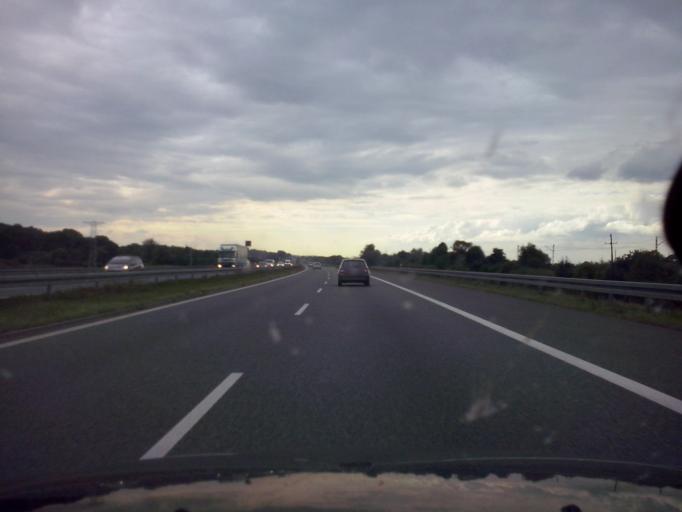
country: PL
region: Lesser Poland Voivodeship
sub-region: Powiat wielicki
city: Wegrzce Wielkie
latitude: 50.0187
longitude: 20.1306
